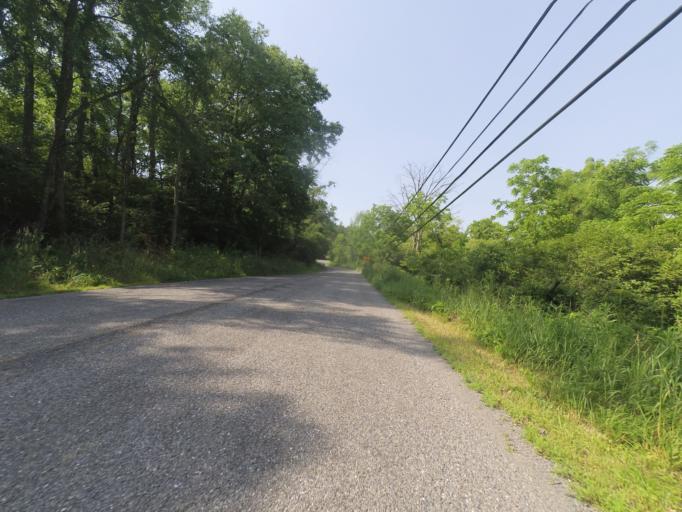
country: US
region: Pennsylvania
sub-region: Centre County
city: Milesburg
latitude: 40.9680
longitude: -77.7408
